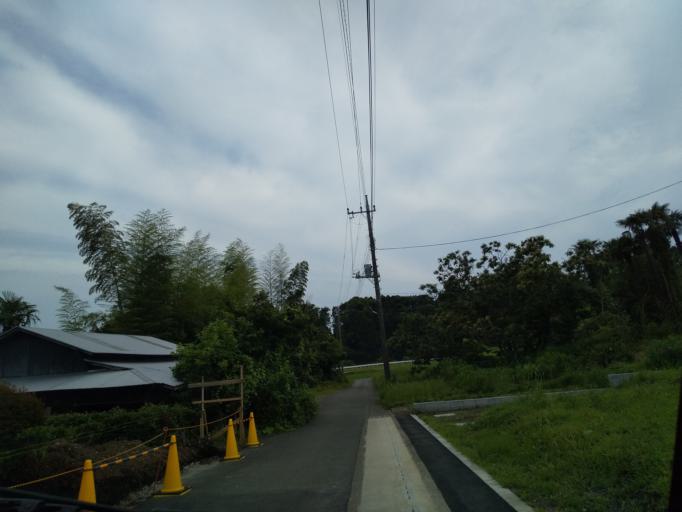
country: JP
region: Kanagawa
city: Atsugi
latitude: 35.4842
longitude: 139.3266
